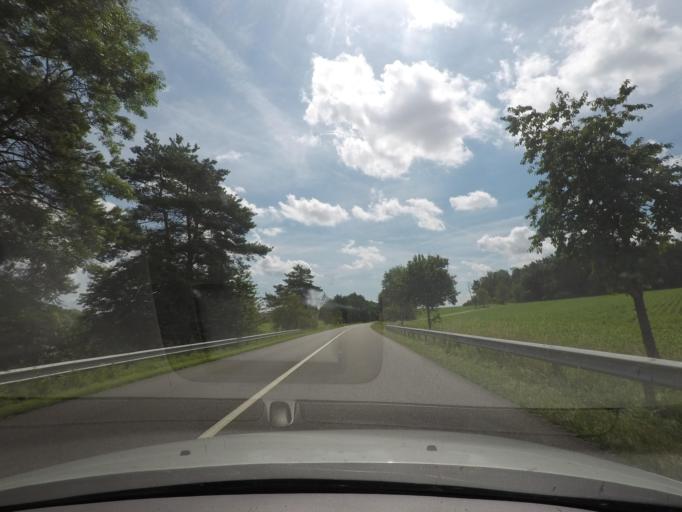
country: FR
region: Alsace
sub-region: Departement du Bas-Rhin
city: Drulingen
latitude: 48.8701
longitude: 7.1713
